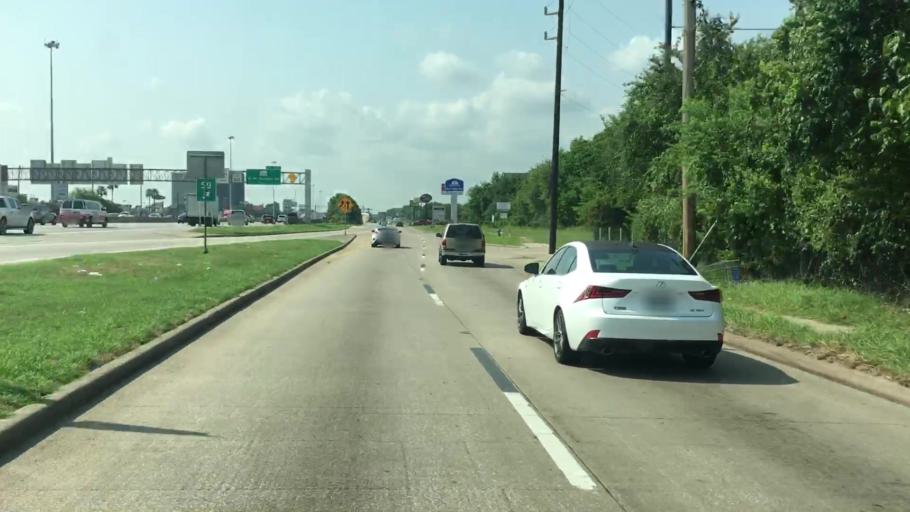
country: US
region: Texas
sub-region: Harris County
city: Aldine
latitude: 29.9307
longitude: -95.4095
